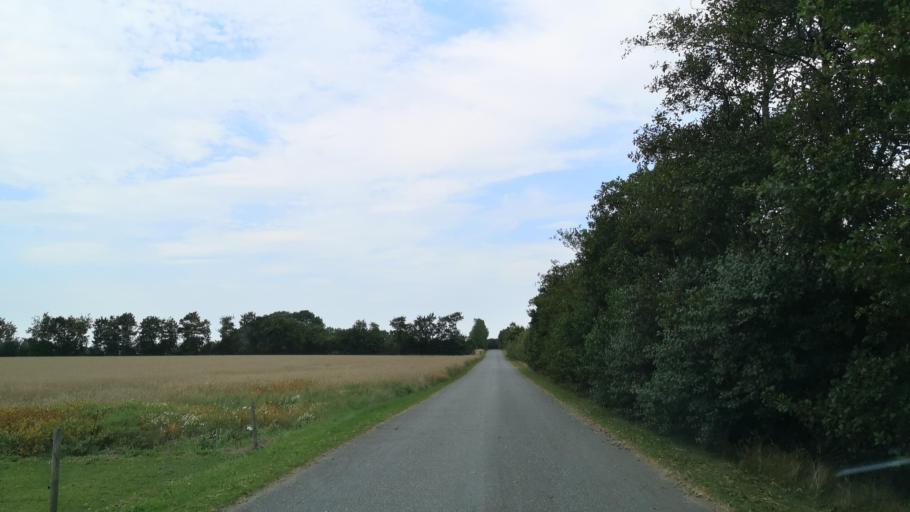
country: DK
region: Central Jutland
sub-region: Ringkobing-Skjern Kommune
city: Videbaek
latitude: 56.0738
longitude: 8.6814
